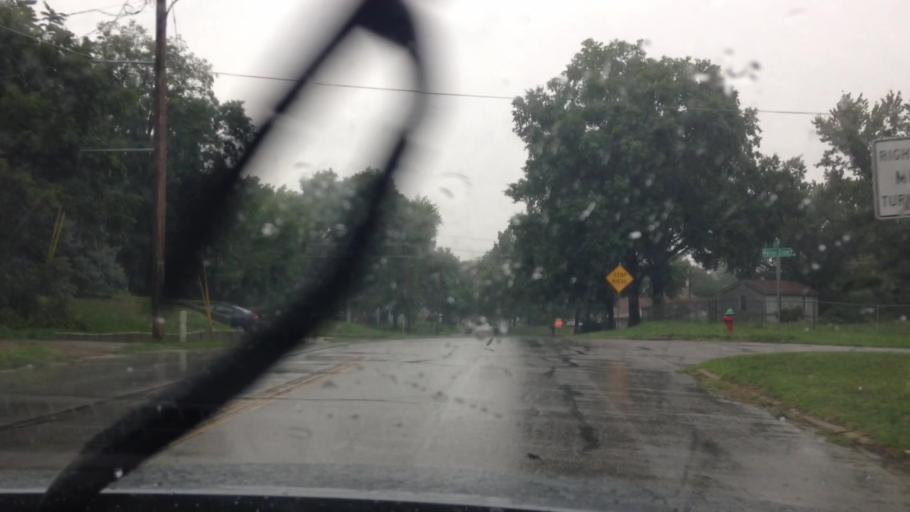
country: US
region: Kansas
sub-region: Leavenworth County
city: Leavenworth
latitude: 39.2948
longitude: -94.9184
